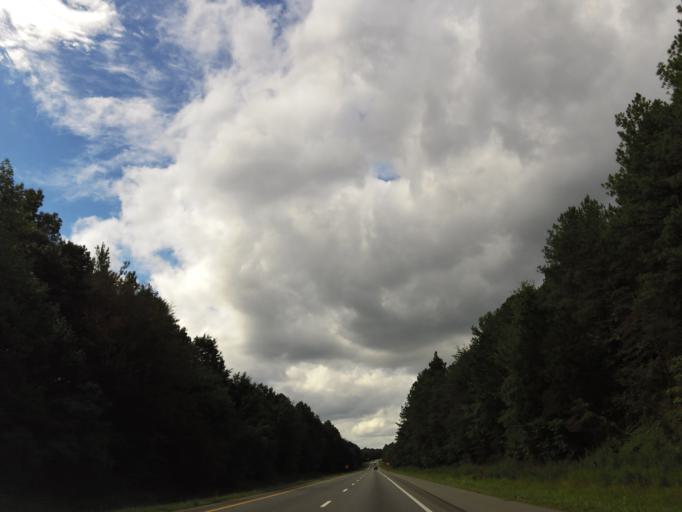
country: US
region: Tennessee
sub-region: Meigs County
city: Decatur
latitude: 35.3716
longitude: -84.7360
